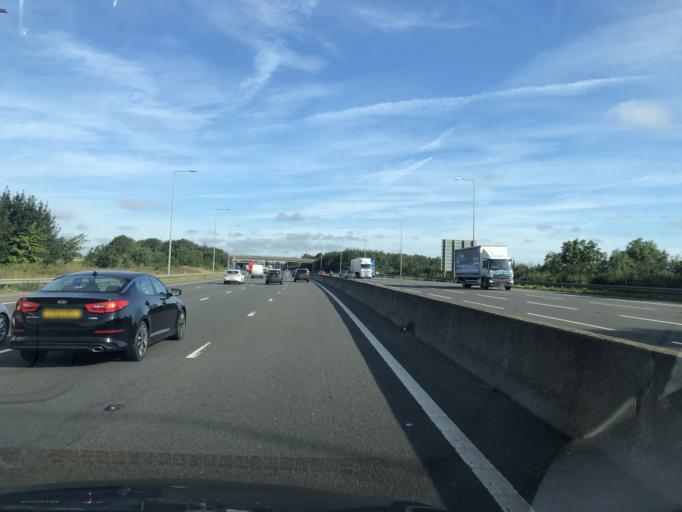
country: GB
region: England
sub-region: Nottinghamshire
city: Kimberley
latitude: 53.0037
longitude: -1.2322
